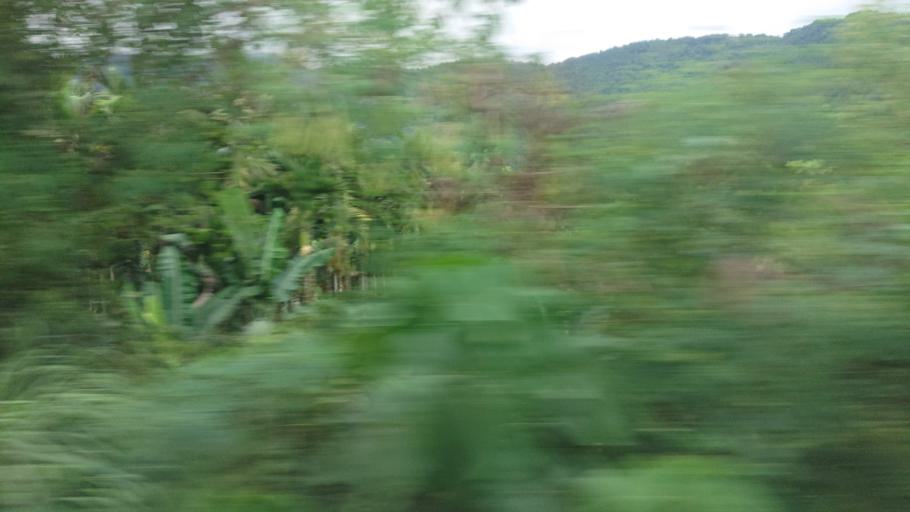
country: TW
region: Taiwan
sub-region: Hualien
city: Hualian
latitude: 23.6628
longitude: 121.4198
